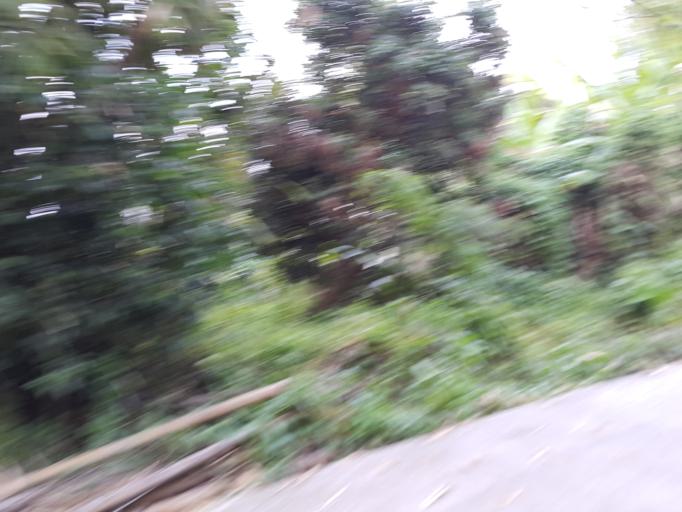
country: TH
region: Chiang Mai
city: San Sai
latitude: 18.8917
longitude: 99.1359
